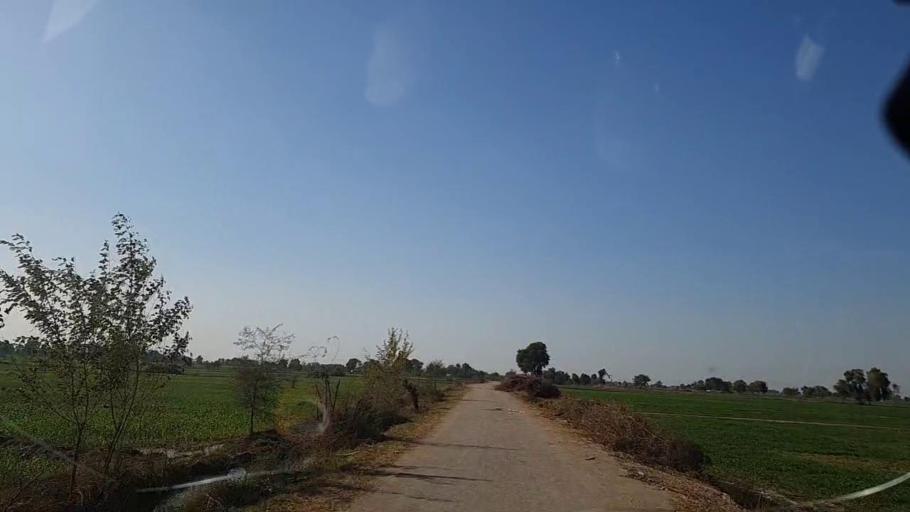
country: PK
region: Sindh
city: Khanpur
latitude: 27.7773
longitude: 69.3622
